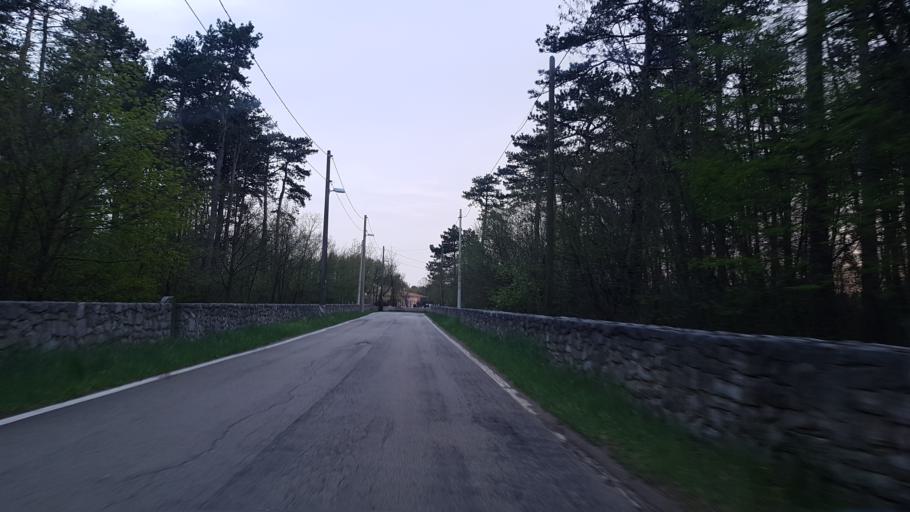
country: IT
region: Friuli Venezia Giulia
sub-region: Provincia di Trieste
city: Domio
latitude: 45.6486
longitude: 13.8389
